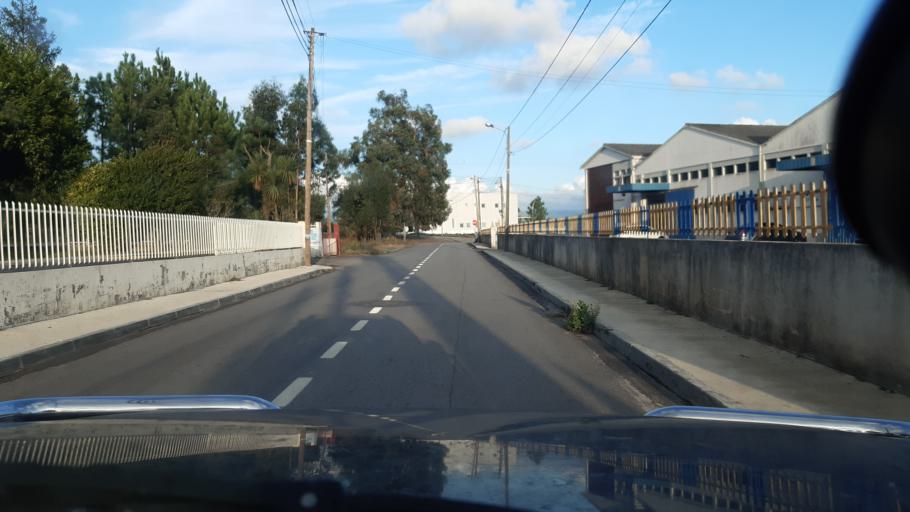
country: PT
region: Aveiro
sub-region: Agueda
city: Agueda
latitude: 40.5818
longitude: -8.4653
